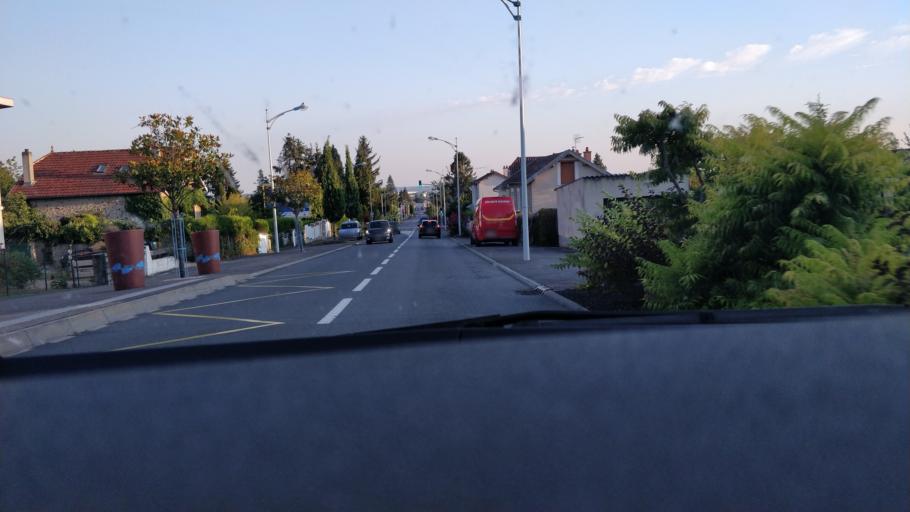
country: FR
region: Limousin
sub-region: Departement de la Haute-Vienne
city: Couzeix
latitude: 45.8687
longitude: 1.2383
